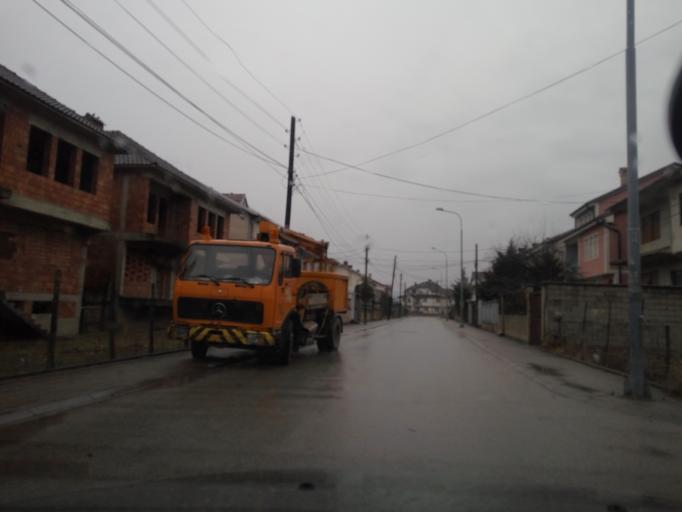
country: XK
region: Gjakova
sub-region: Komuna e Gjakoves
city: Gjakove
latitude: 42.3655
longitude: 20.4406
